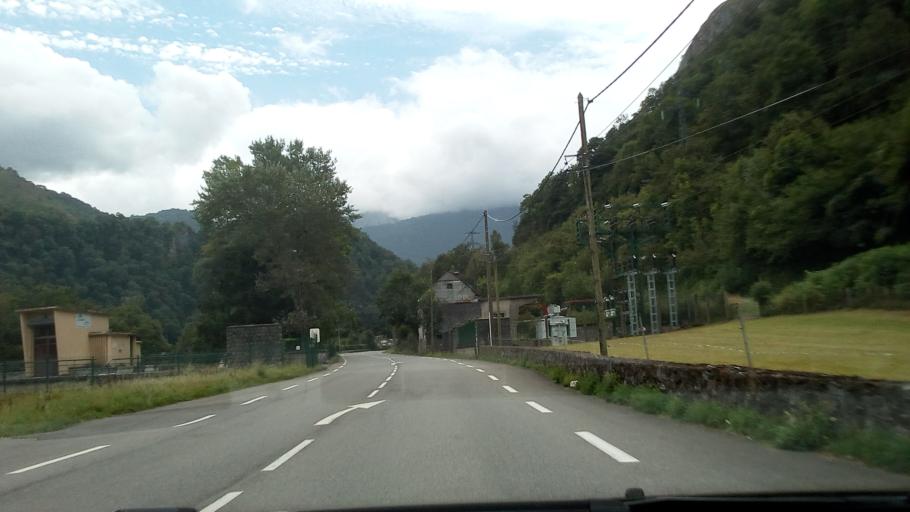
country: FR
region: Aquitaine
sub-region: Departement des Pyrenees-Atlantiques
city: Laruns
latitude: 43.0103
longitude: -0.4222
